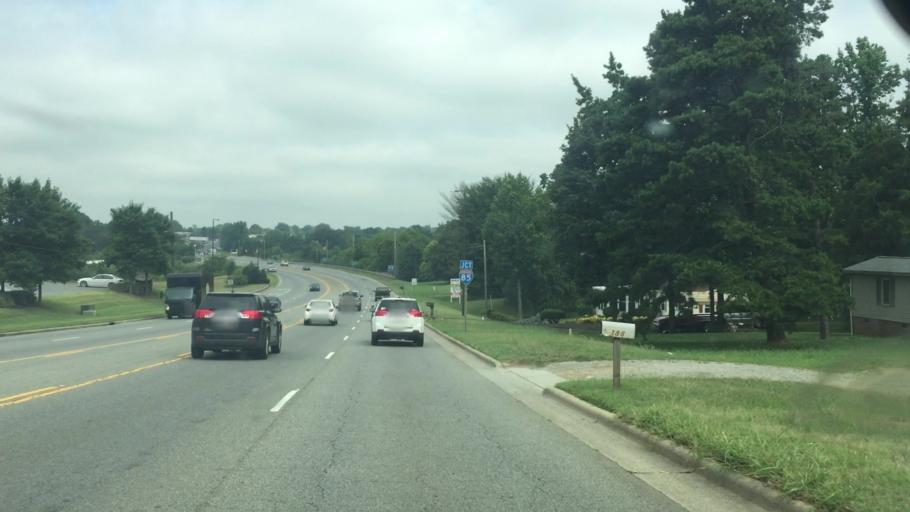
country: US
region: North Carolina
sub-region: Cabarrus County
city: Kannapolis
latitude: 35.4161
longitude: -80.6686
